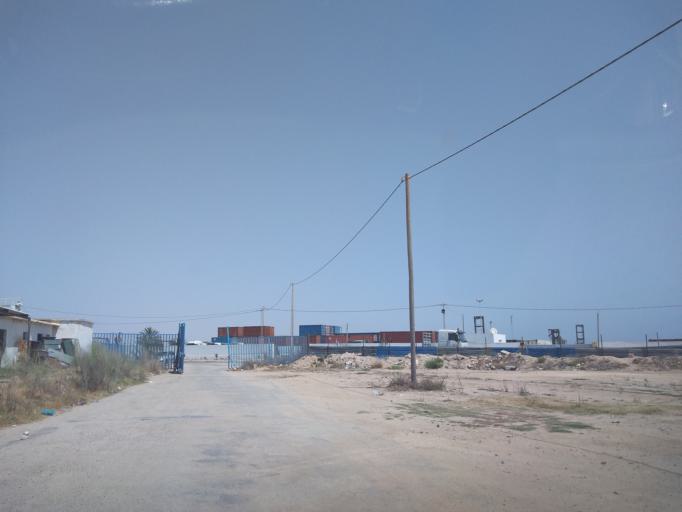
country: TN
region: Safaqis
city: Al Qarmadah
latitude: 34.7283
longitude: 10.7797
